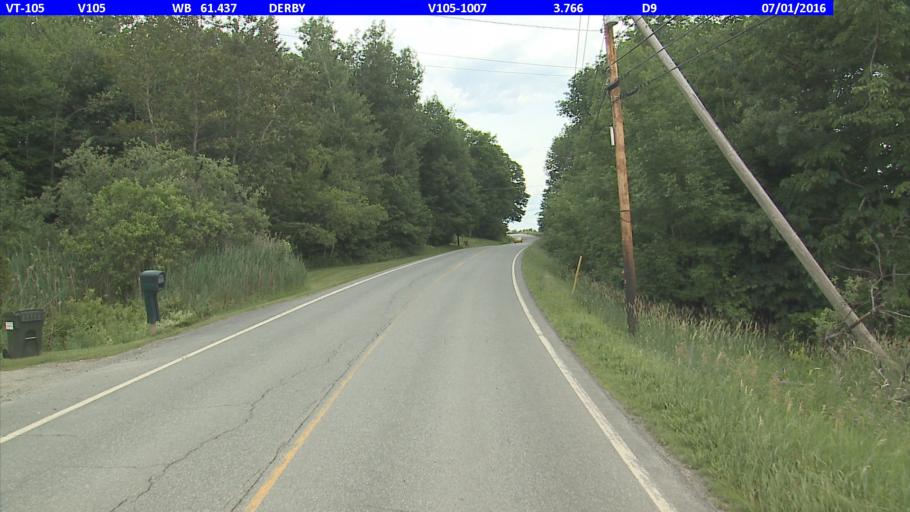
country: US
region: Vermont
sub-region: Orleans County
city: Newport
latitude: 44.9113
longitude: -72.0958
